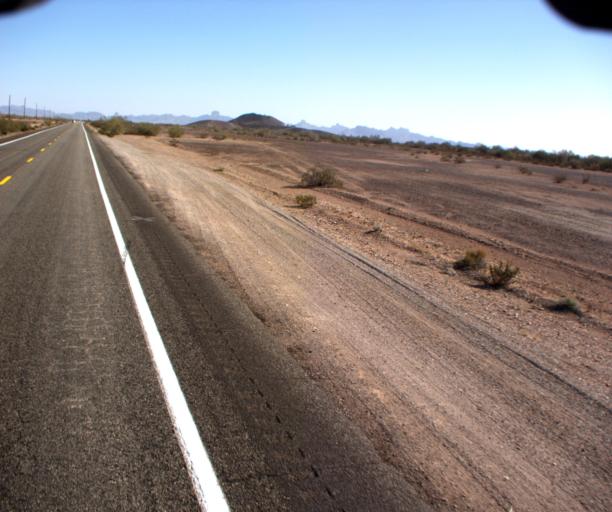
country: US
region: Arizona
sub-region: Yuma County
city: Fortuna Foothills
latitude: 32.9116
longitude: -114.3259
